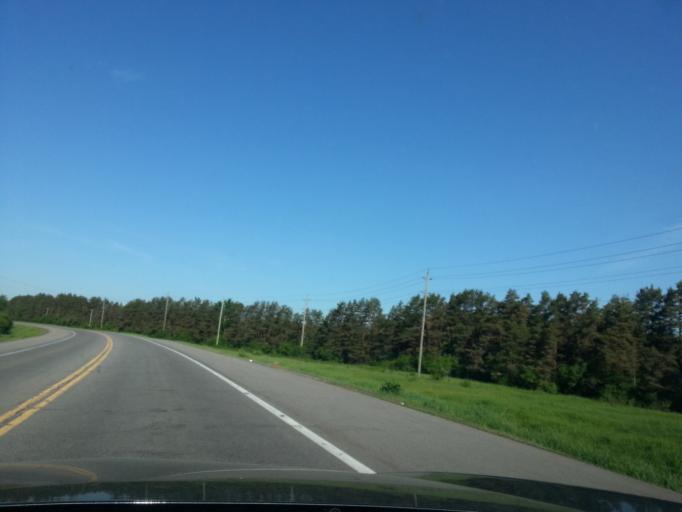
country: CA
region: Ontario
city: Bells Corners
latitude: 45.3554
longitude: -75.8551
